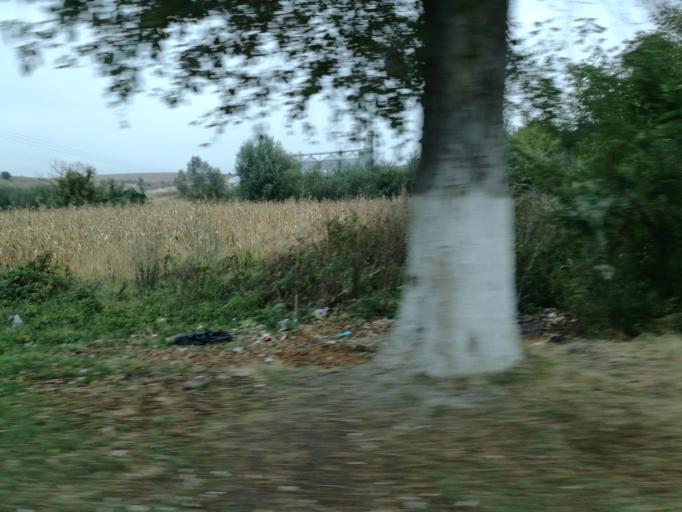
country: RO
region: Tulcea
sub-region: Comuna Ciucurova
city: Ciucurova
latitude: 44.9268
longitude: 28.4474
